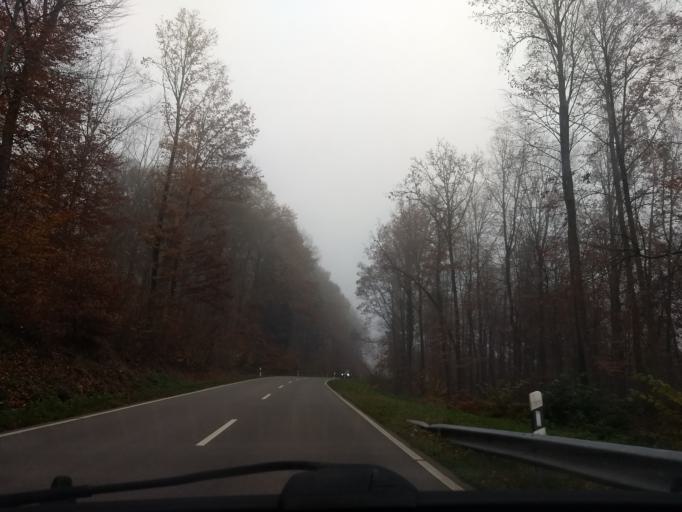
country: DE
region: Baden-Wuerttemberg
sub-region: Karlsruhe Region
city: Kuppenheim
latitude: 48.8118
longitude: 8.2439
